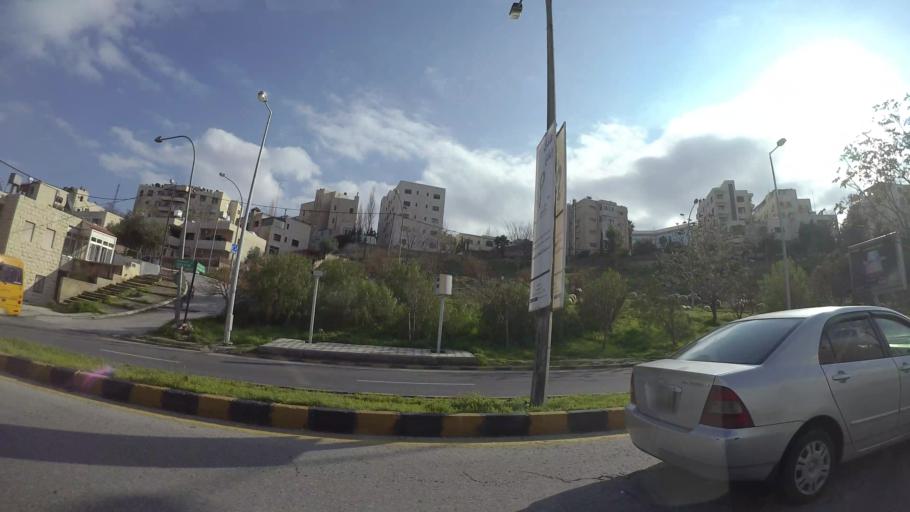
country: JO
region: Amman
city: Amman
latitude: 31.9594
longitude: 35.9006
